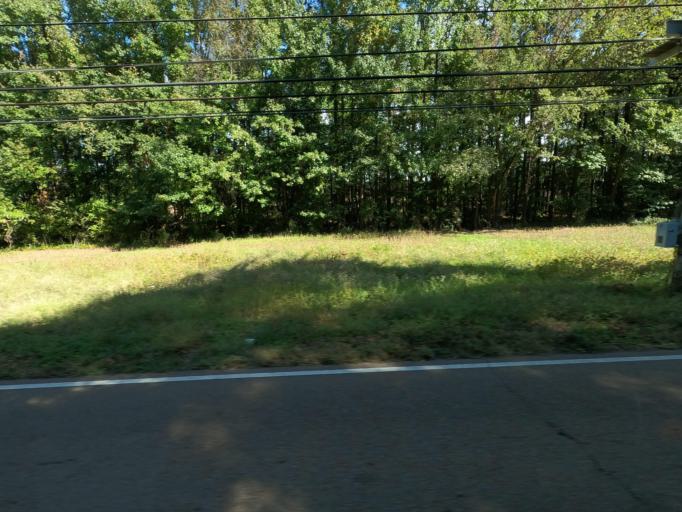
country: US
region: Tennessee
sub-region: Fayette County
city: Hickory Withe
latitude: 35.2304
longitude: -89.6500
